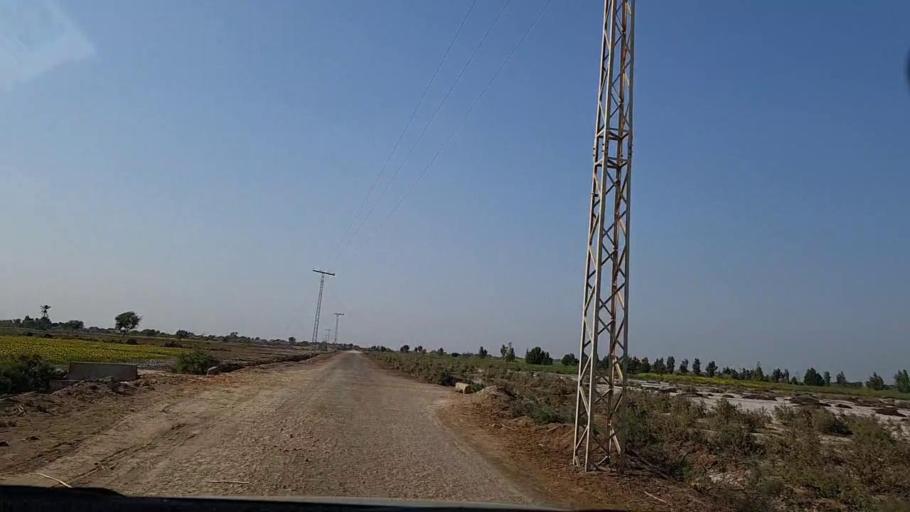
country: PK
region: Sindh
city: Digri
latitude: 25.1716
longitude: 69.0182
